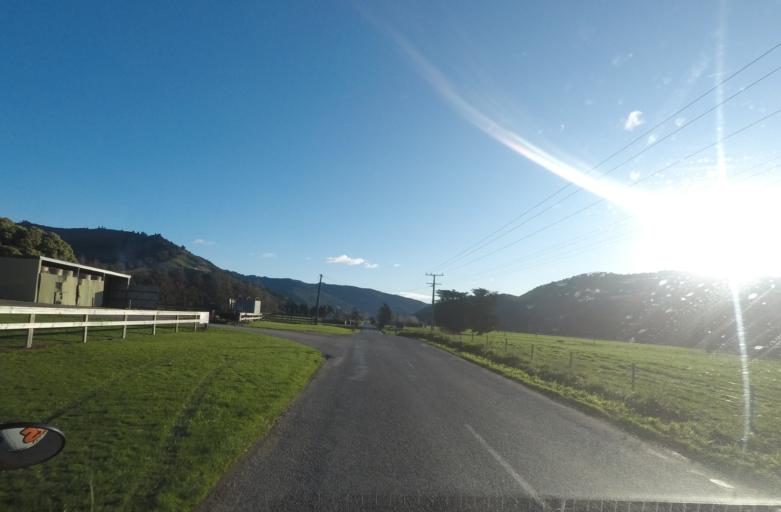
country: NZ
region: Marlborough
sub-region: Marlborough District
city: Picton
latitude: -41.2894
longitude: 173.8648
